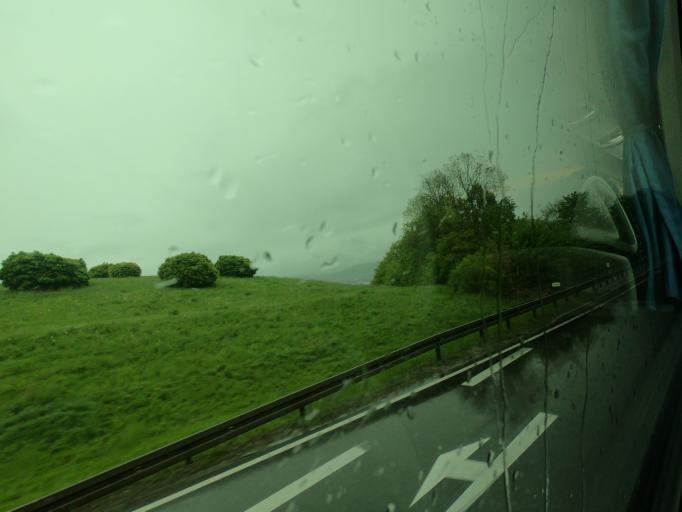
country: DE
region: Baden-Wuerttemberg
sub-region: Regierungsbezirk Stuttgart
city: Aalen
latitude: 48.8275
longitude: 10.0747
